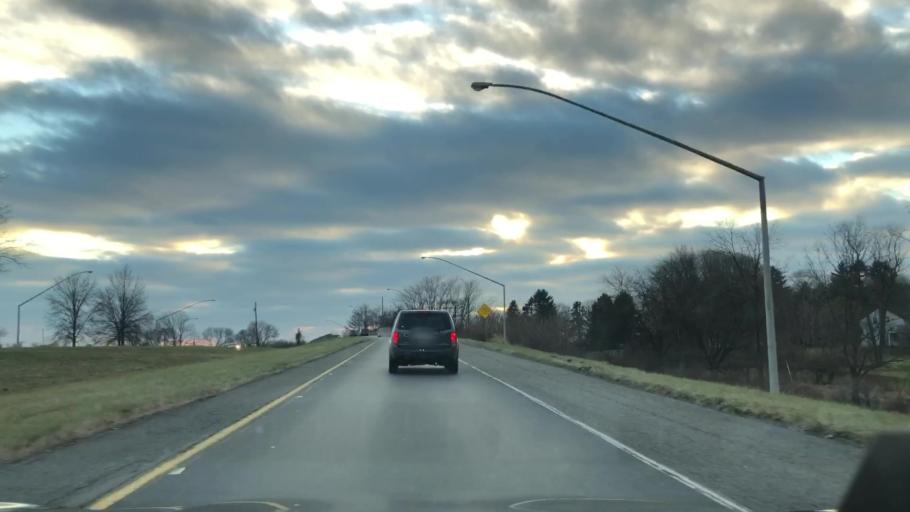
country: US
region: Pennsylvania
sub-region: Northampton County
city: Palmer Heights
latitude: 40.6866
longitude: -75.2901
